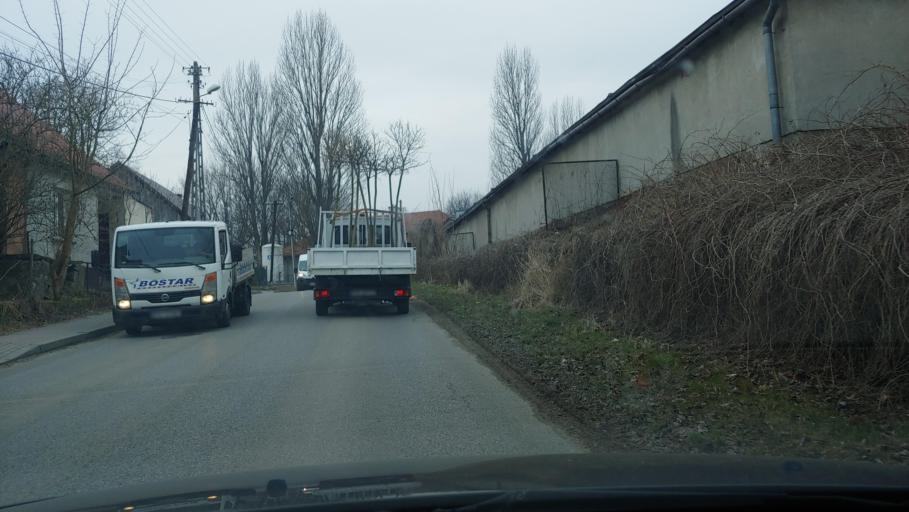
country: PL
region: Lesser Poland Voivodeship
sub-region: Powiat krakowski
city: Balice
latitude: 50.0862
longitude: 19.7906
